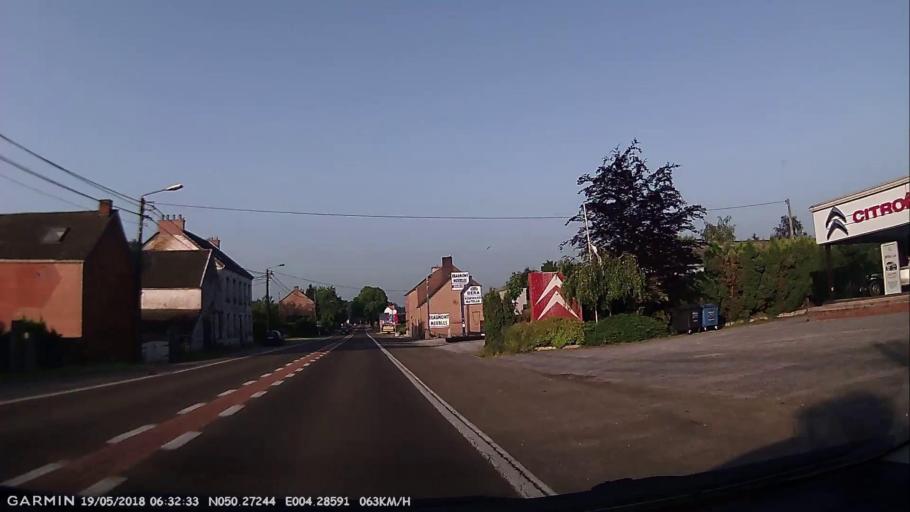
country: BE
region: Wallonia
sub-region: Province du Hainaut
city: Beaumont
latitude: 50.2725
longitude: 4.2859
